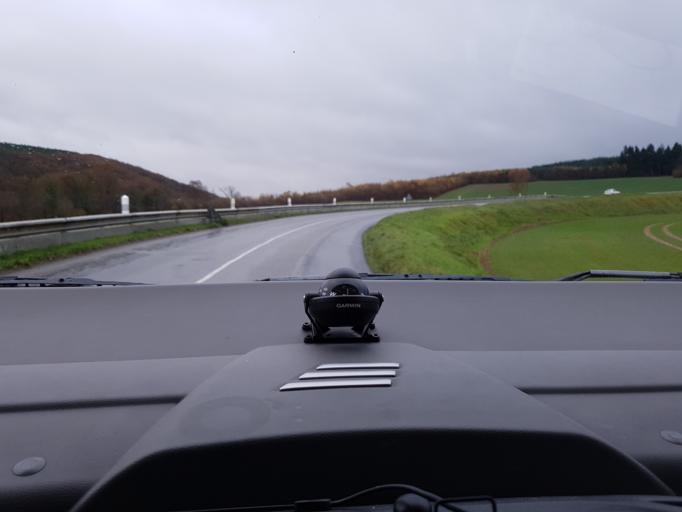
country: FR
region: Haute-Normandie
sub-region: Departement de l'Eure
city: Pont-Saint-Pierre
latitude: 49.3327
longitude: 1.2977
